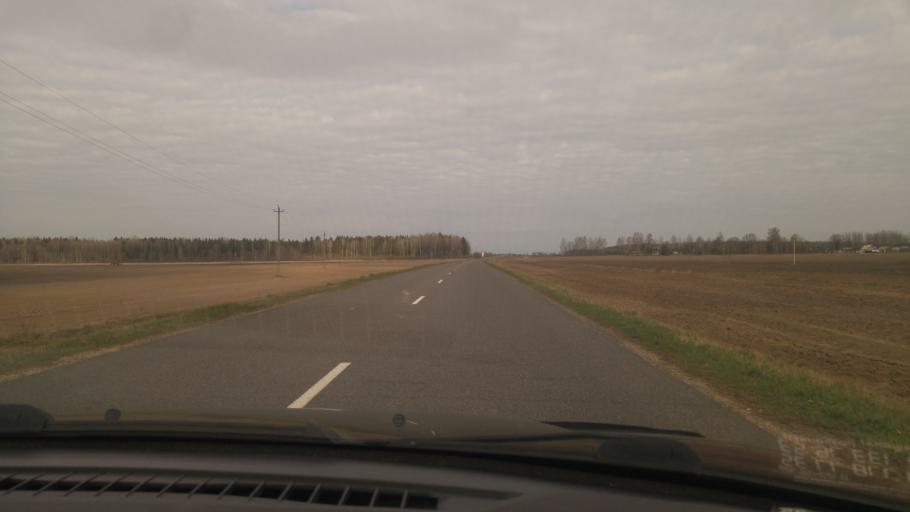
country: BY
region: Minsk
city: Chervyen'
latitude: 53.6216
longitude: 28.6752
